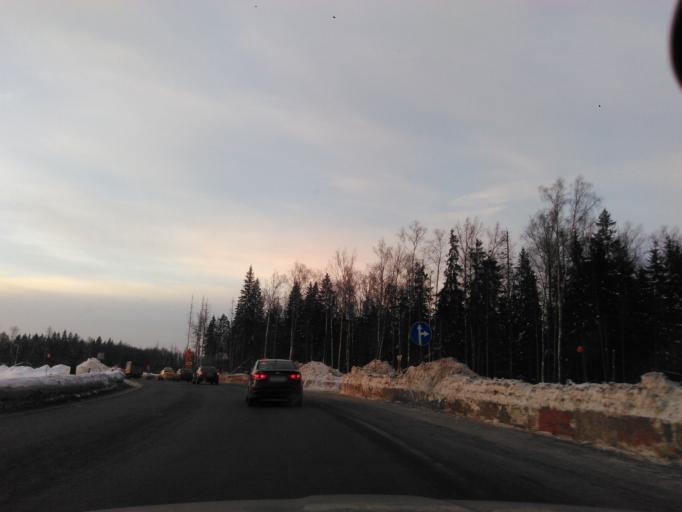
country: RU
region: Moskovskaya
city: Povarovo
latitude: 56.0052
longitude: 37.0239
